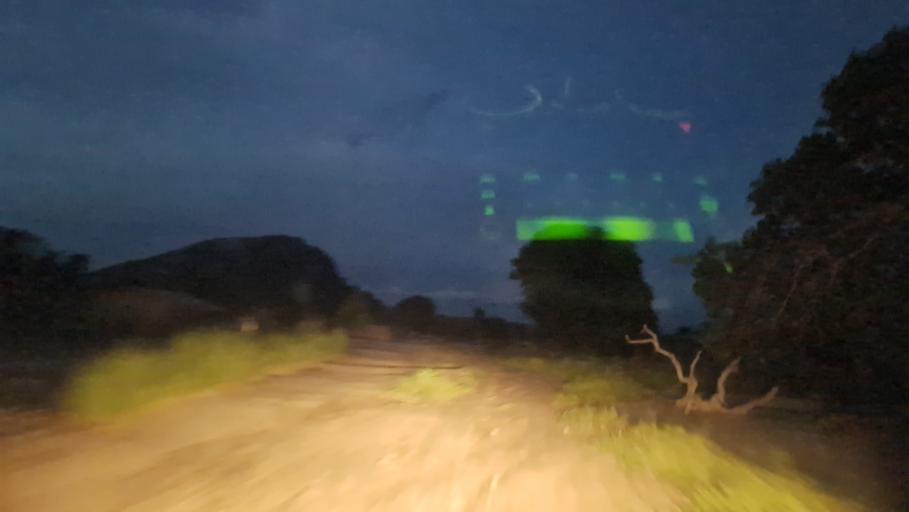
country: MZ
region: Nampula
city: Nampula
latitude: -14.6660
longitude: 39.8367
